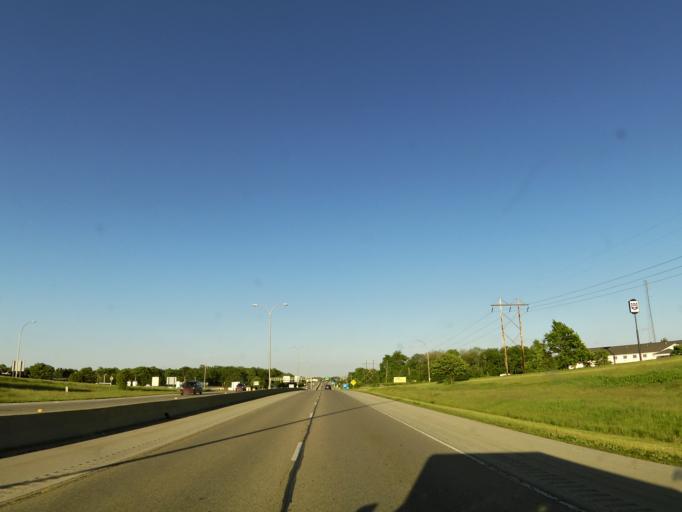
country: US
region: Illinois
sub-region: Champaign County
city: Urbana
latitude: 40.1350
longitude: -88.2192
